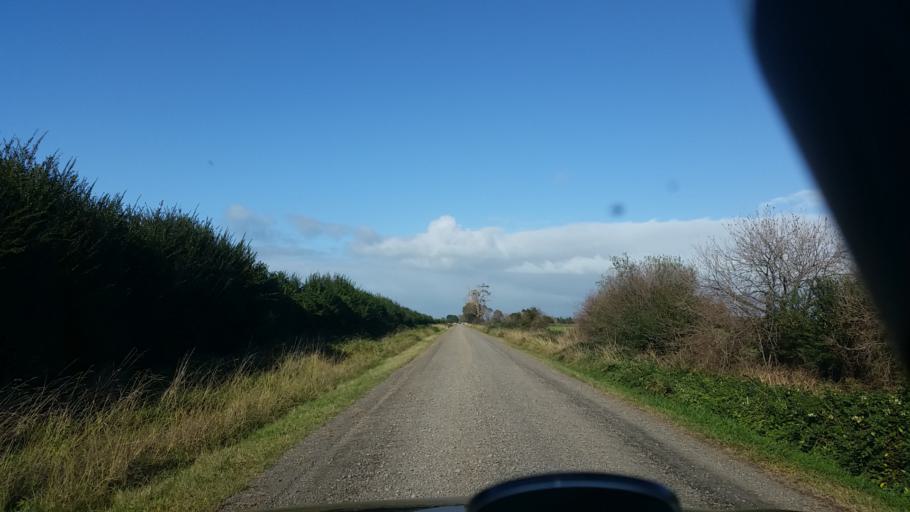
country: NZ
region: Bay of Plenty
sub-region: Western Bay of Plenty District
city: Katikati
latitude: -37.5828
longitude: 175.7131
